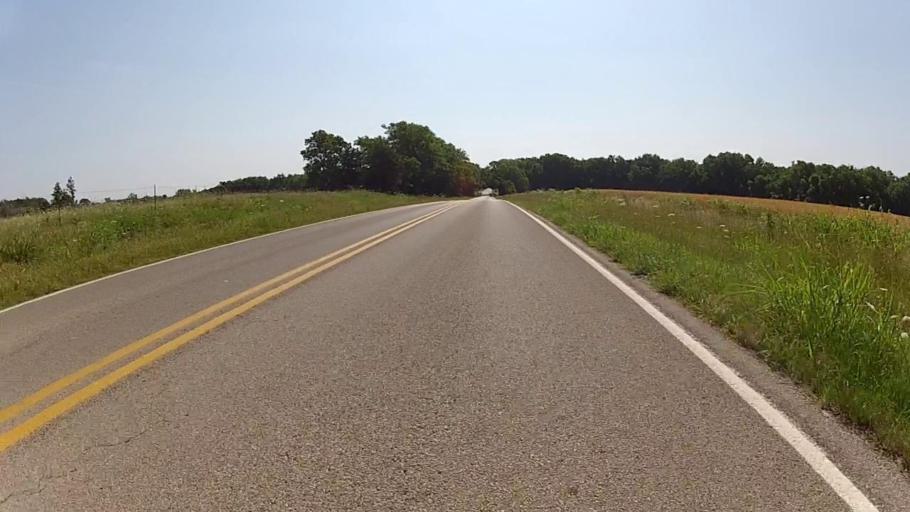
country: US
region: Kansas
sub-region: Montgomery County
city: Independence
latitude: 37.1930
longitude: -95.7373
